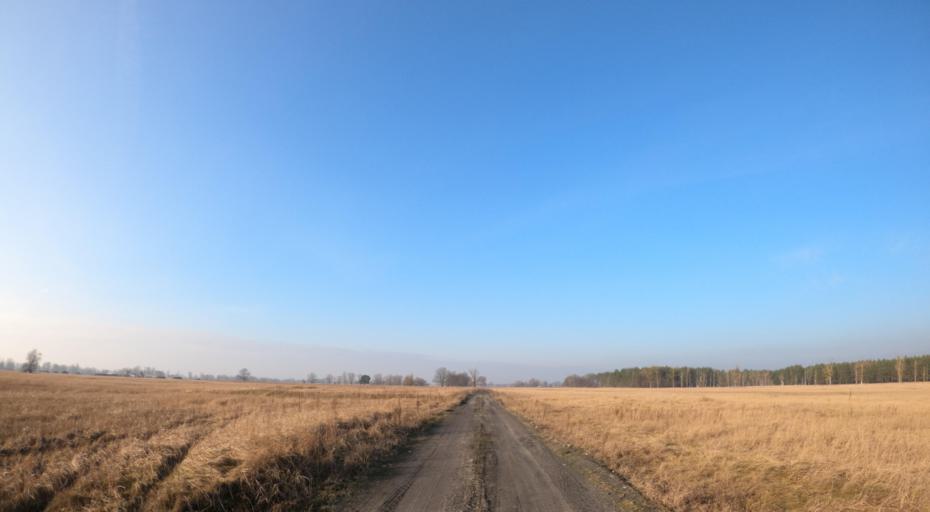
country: DE
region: Brandenburg
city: Zechin
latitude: 52.6518
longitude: 14.5117
